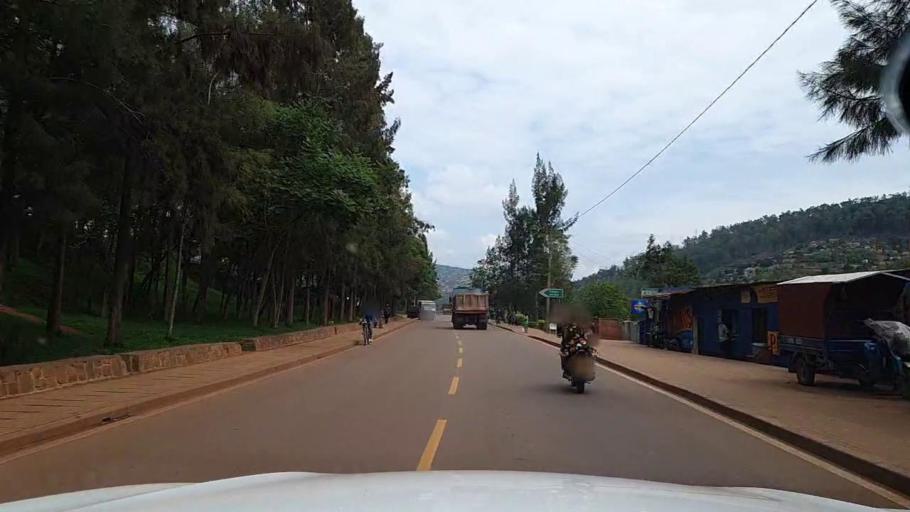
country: RW
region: Kigali
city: Kigali
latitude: -1.9207
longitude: 30.0476
